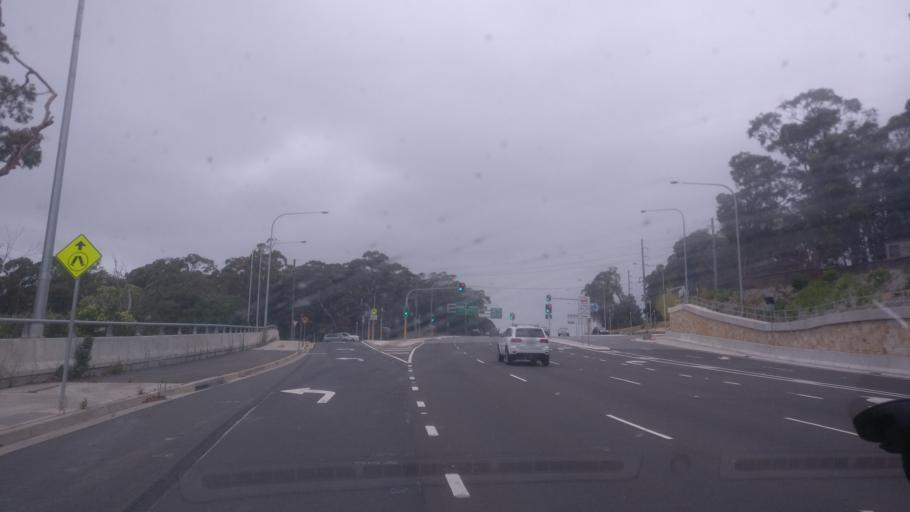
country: AU
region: New South Wales
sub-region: Warringah
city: Allambie Heights
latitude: -33.7490
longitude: 151.2350
